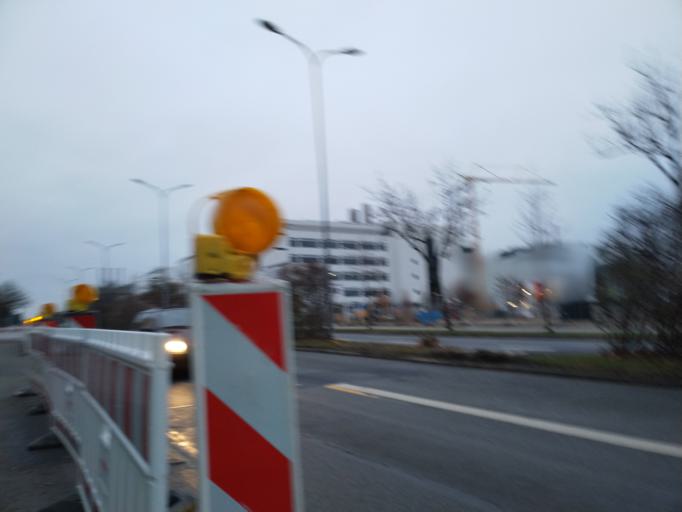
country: DE
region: Bavaria
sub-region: Upper Bavaria
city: Oberschleissheim
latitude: 48.1933
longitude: 11.5651
